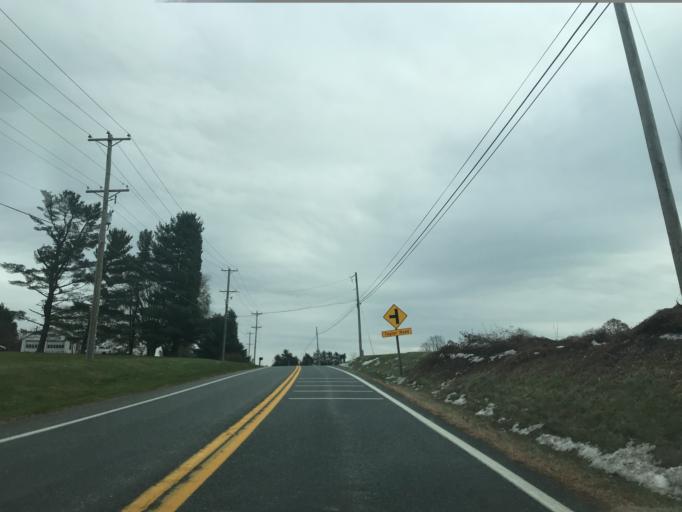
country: US
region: Pennsylvania
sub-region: York County
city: Susquehanna Trails
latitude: 39.6674
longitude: -76.3515
